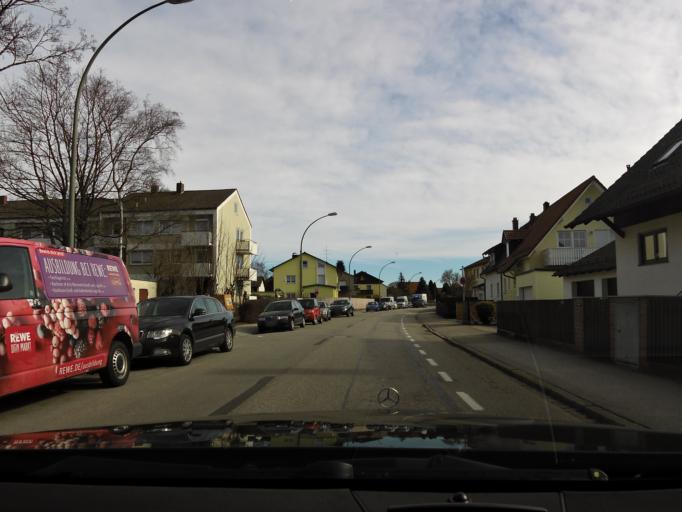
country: DE
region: Bavaria
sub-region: Lower Bavaria
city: Landshut
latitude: 48.5534
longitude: 12.1274
